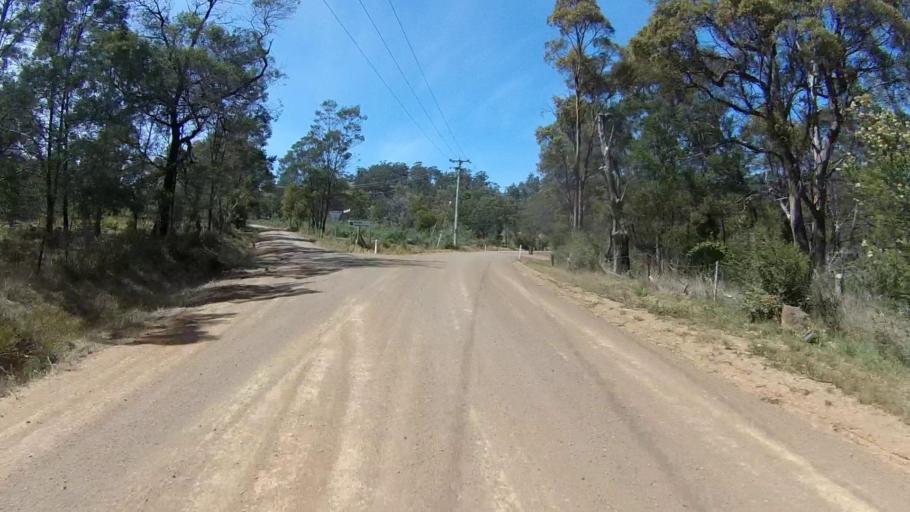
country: AU
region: Tasmania
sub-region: Sorell
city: Sorell
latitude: -42.7667
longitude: 147.6515
